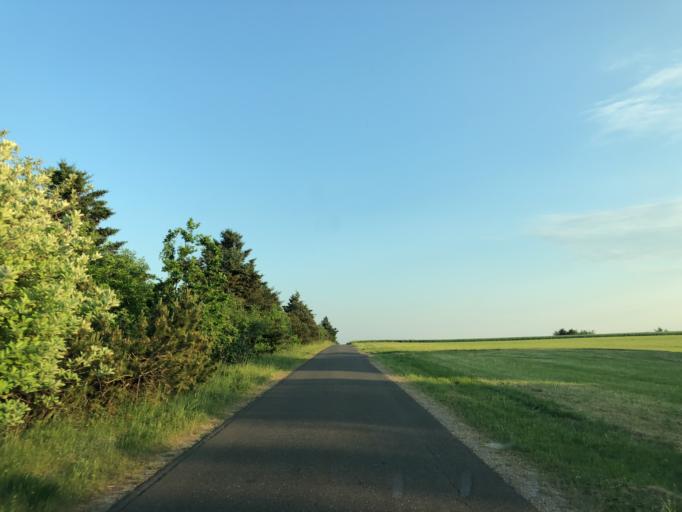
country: DK
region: Central Jutland
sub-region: Struer Kommune
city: Struer
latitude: 56.4095
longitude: 8.4882
